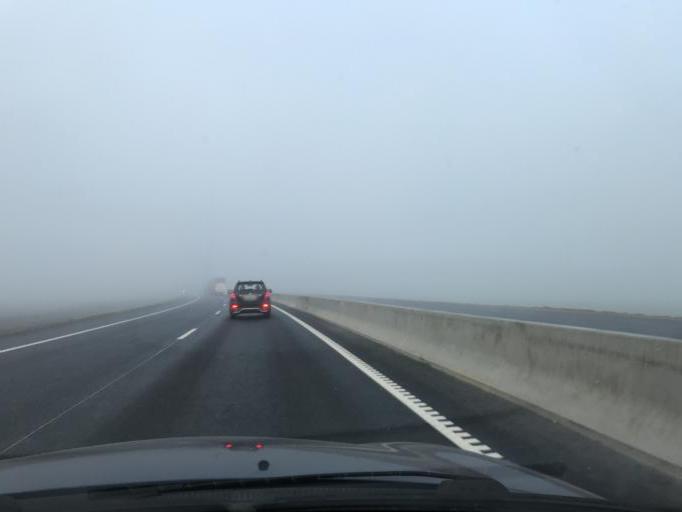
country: BY
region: Minsk
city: Valozhyn
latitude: 54.0659
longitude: 26.5187
